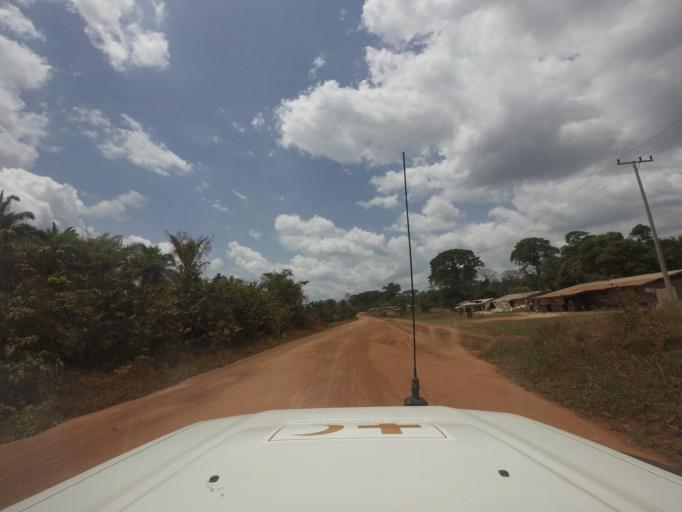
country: LR
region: Nimba
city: Sanniquellie
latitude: 7.2360
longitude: -8.9619
